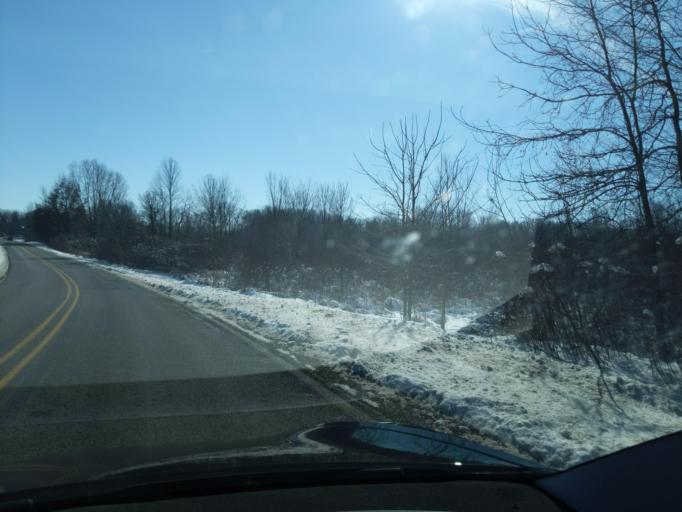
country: US
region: Michigan
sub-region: Livingston County
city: Fowlerville
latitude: 42.5785
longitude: -84.0743
